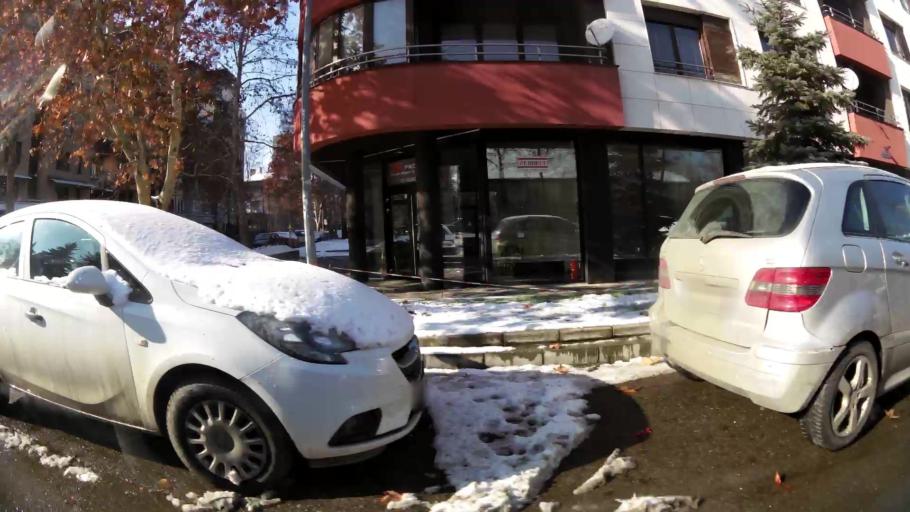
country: BG
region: Sofia-Capital
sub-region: Stolichna Obshtina
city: Sofia
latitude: 42.6770
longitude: 23.3118
